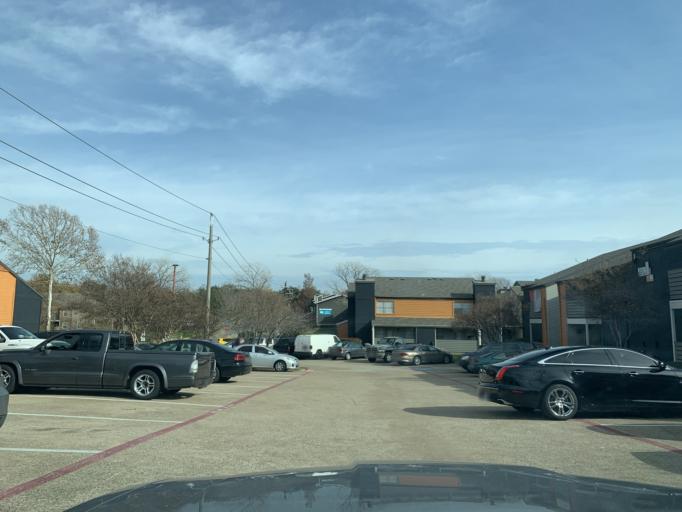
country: US
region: Texas
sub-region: Tarrant County
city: Euless
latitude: 32.7821
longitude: -97.0656
